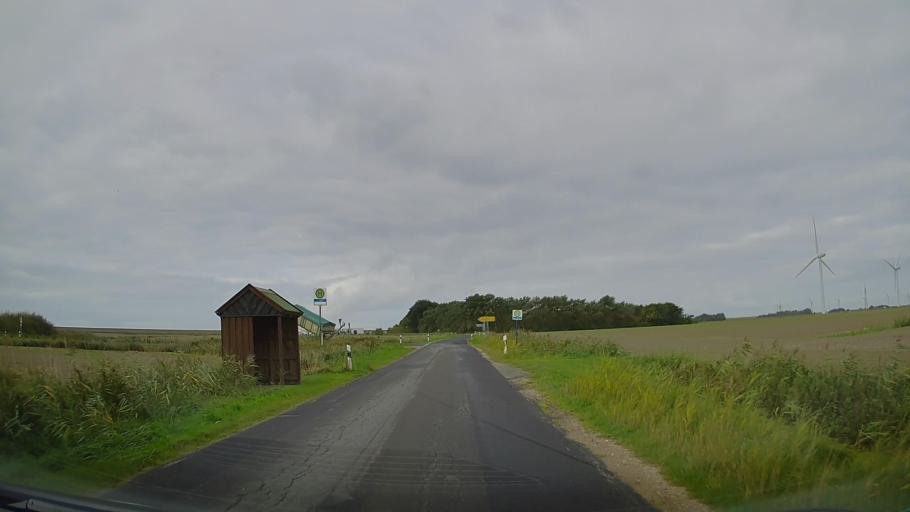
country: DE
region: Schleswig-Holstein
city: Emmelsbull-Horsbull
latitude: 54.8070
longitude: 8.6680
